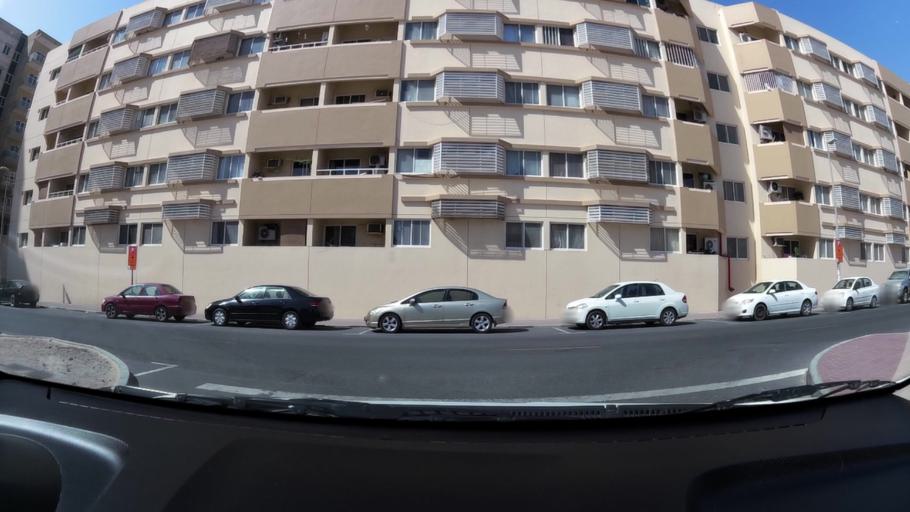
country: AE
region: Ash Shariqah
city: Sharjah
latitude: 25.2737
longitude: 55.3750
